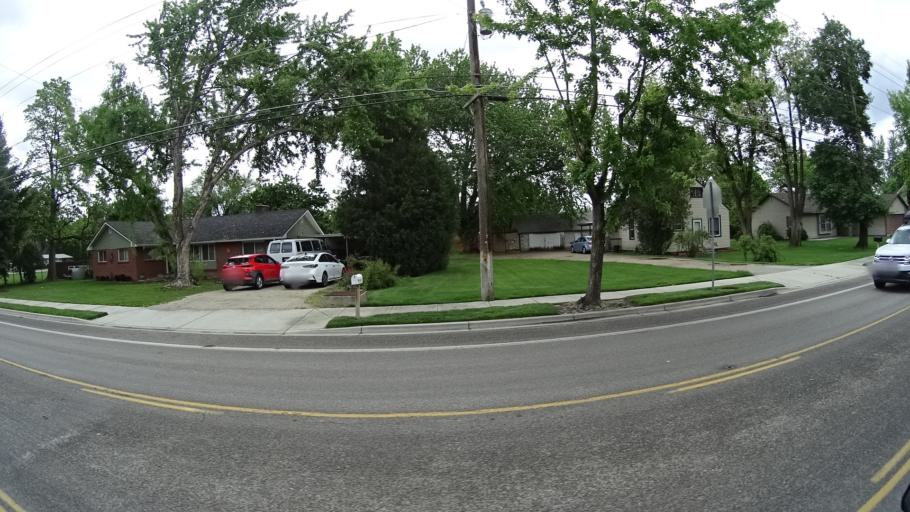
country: US
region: Idaho
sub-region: Ada County
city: Eagle
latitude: 43.6976
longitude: -116.3540
